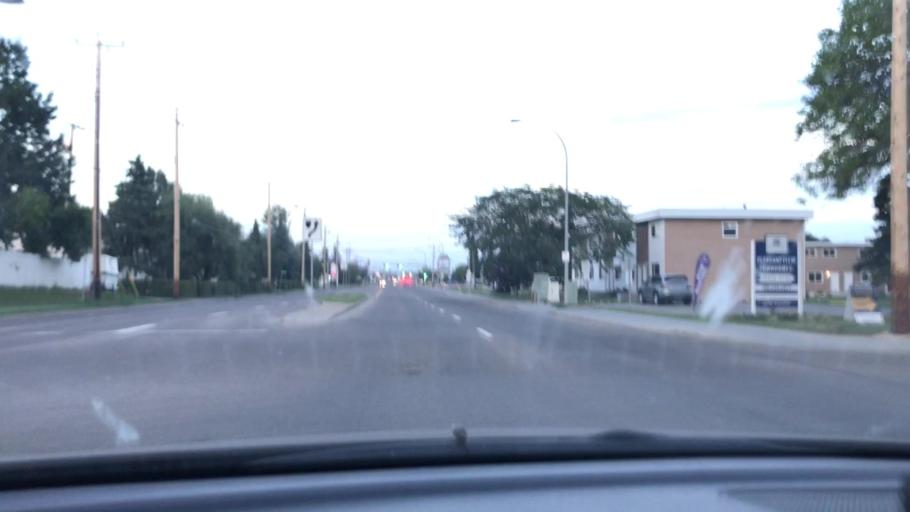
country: CA
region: Alberta
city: Edmonton
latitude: 53.4882
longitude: -113.5080
